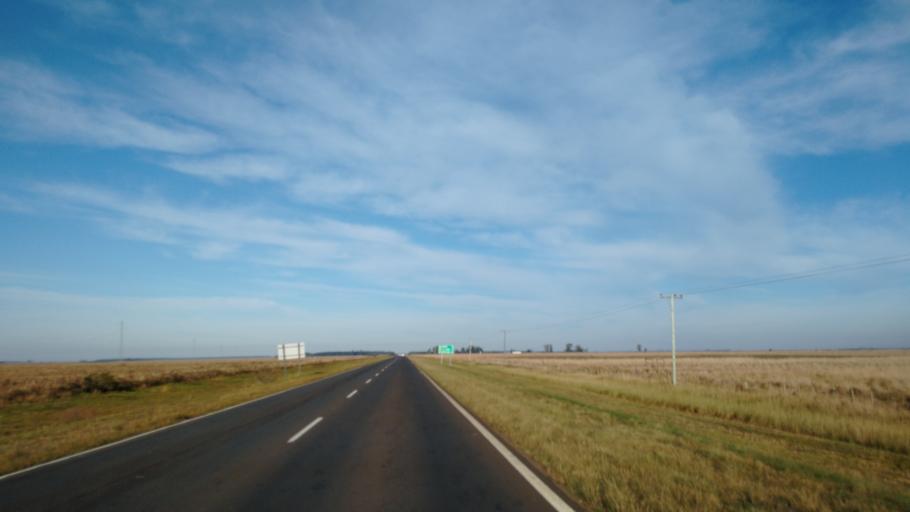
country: AR
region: Corrientes
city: La Cruz
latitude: -29.2251
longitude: -56.7155
